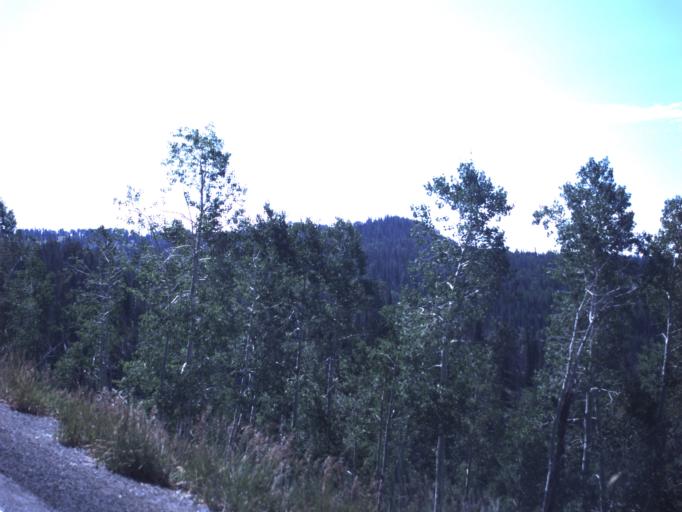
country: US
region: Utah
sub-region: Sanpete County
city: Fairview
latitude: 39.6828
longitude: -111.2387
